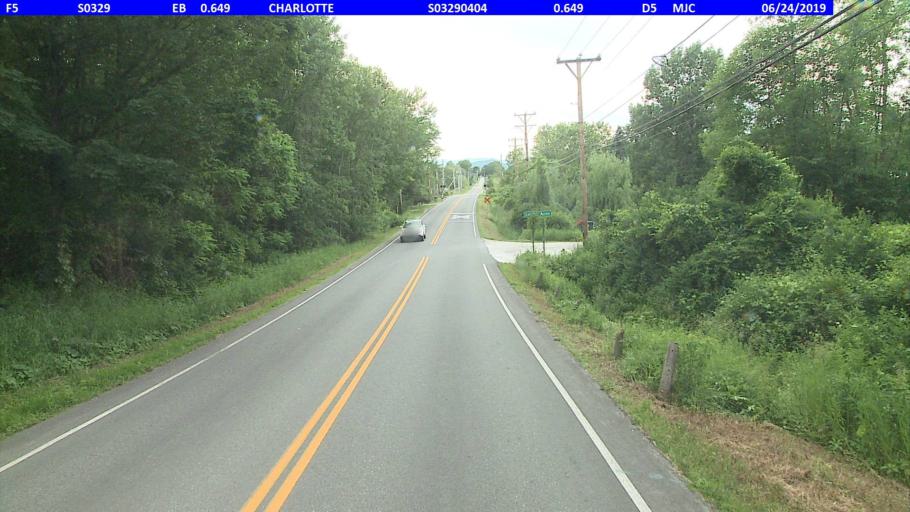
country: US
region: Vermont
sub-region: Addison County
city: Vergennes
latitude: 44.3099
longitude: -73.2592
